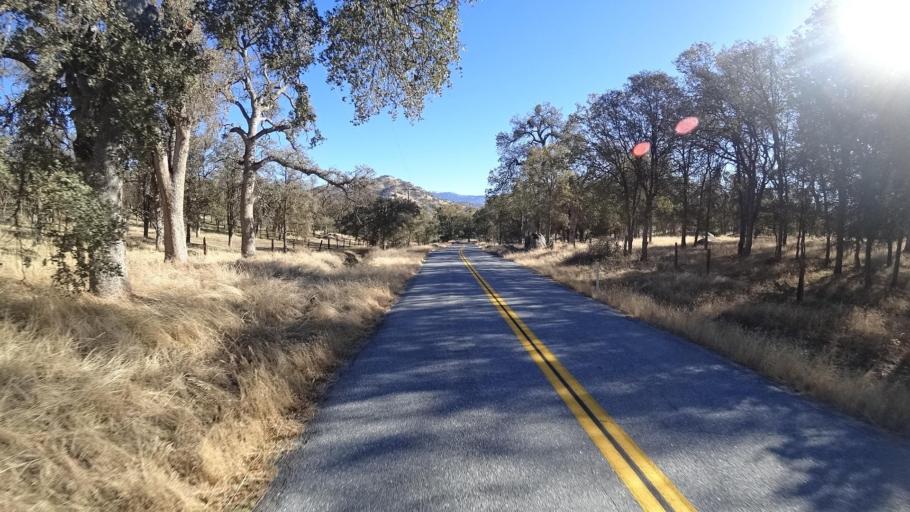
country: US
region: California
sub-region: Kern County
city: Alta Sierra
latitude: 35.7939
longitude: -118.7260
